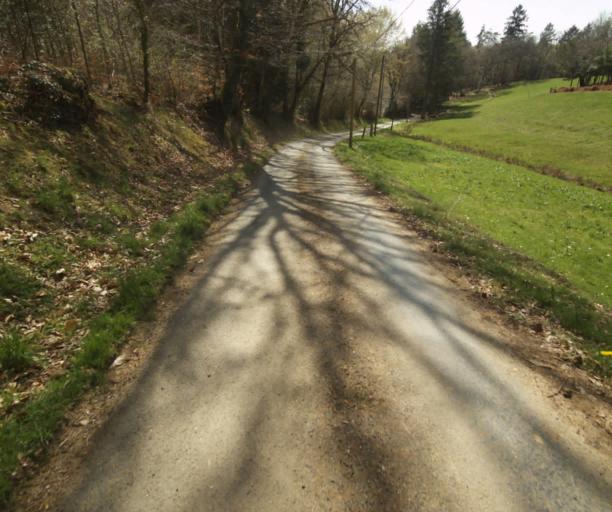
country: FR
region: Limousin
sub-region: Departement de la Correze
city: Seilhac
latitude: 45.4033
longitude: 1.7731
